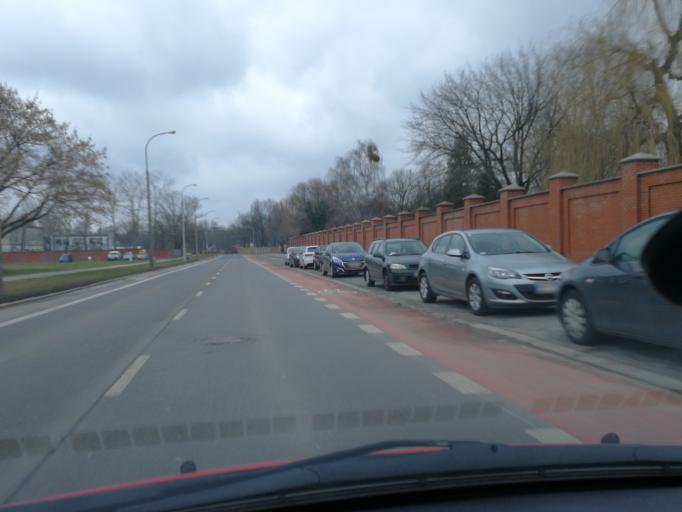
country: PL
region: Masovian Voivodeship
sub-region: Warszawa
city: Wola
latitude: 52.2503
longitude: 20.9650
